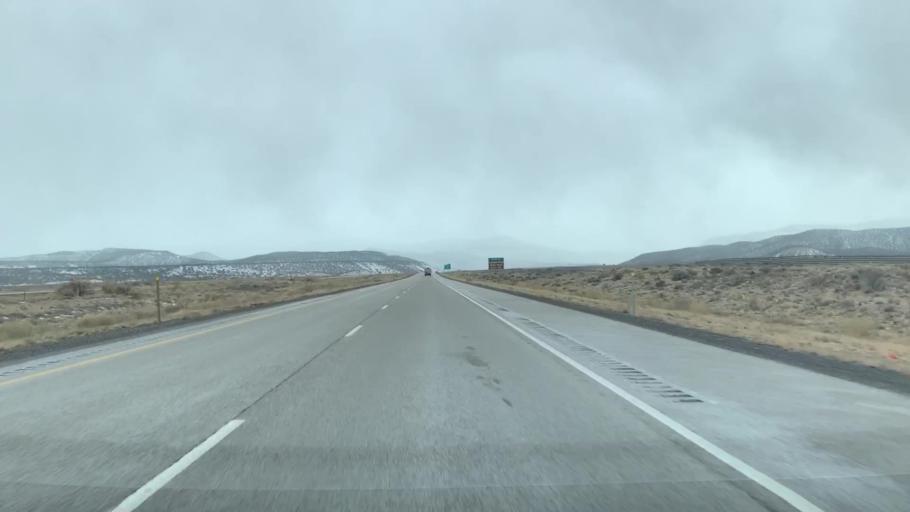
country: US
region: Utah
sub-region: Emery County
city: Ferron
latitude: 38.7738
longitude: -111.3282
